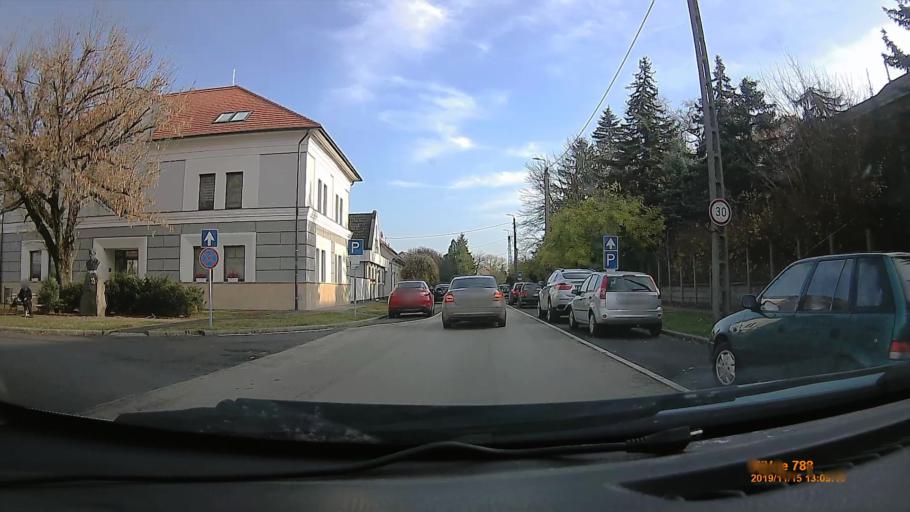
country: HU
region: Bekes
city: Gyula
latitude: 46.6425
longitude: 21.2763
